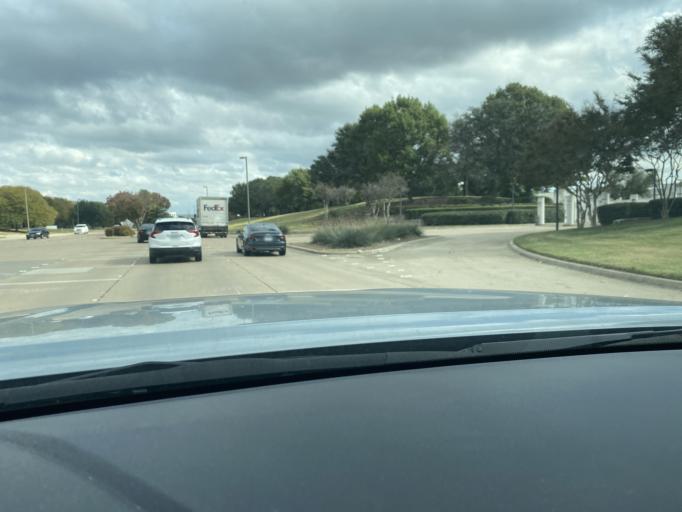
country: US
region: Texas
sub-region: Denton County
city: The Colony
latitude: 33.0779
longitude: -96.8163
